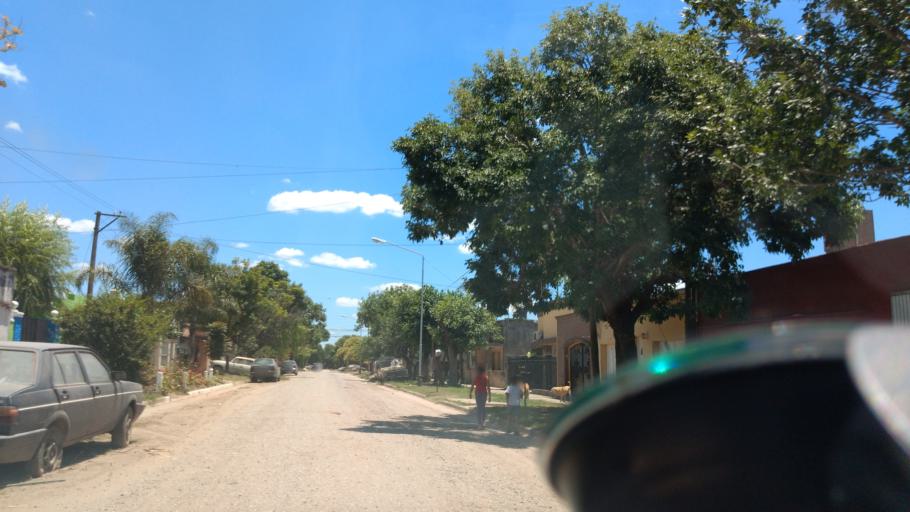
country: AR
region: Santa Fe
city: Laguna Paiva
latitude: -31.3118
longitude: -60.6585
